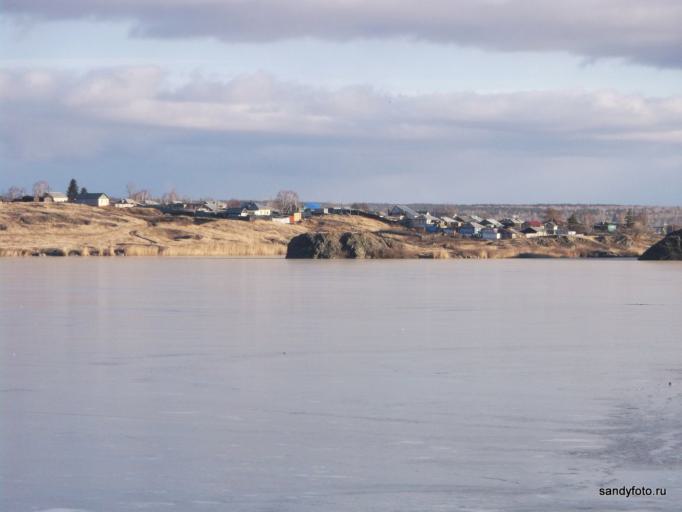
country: RU
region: Chelyabinsk
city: Troitsk
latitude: 54.0787
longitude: 61.5614
